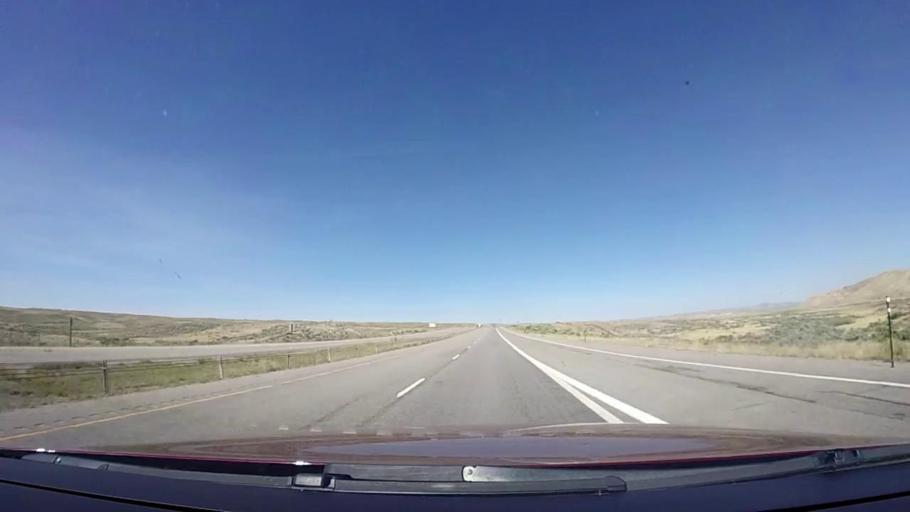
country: US
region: Wyoming
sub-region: Sweetwater County
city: Rock Springs
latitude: 41.6477
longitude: -108.6853
